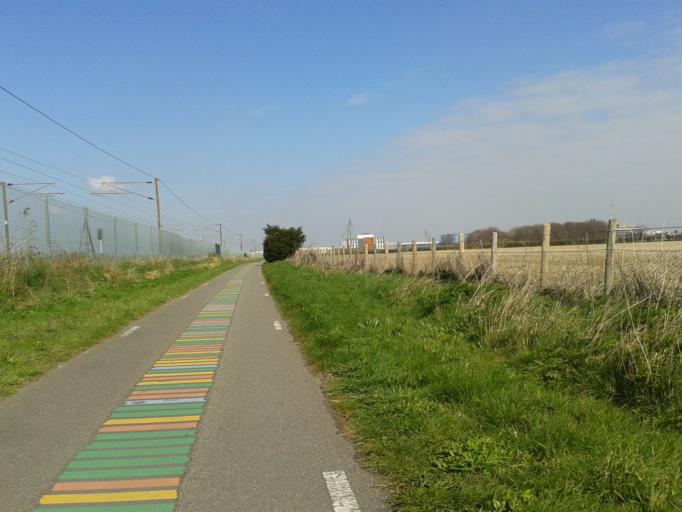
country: GB
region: England
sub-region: Cambridgeshire
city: Cambridge
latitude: 52.1611
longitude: 0.1335
